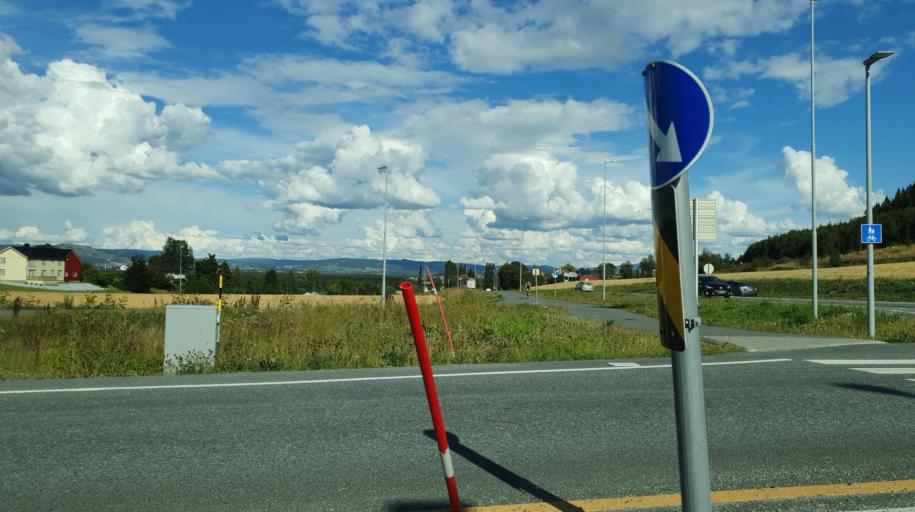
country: NO
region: Nord-Trondelag
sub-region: Verdal
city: Verdal
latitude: 63.7611
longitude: 11.4058
